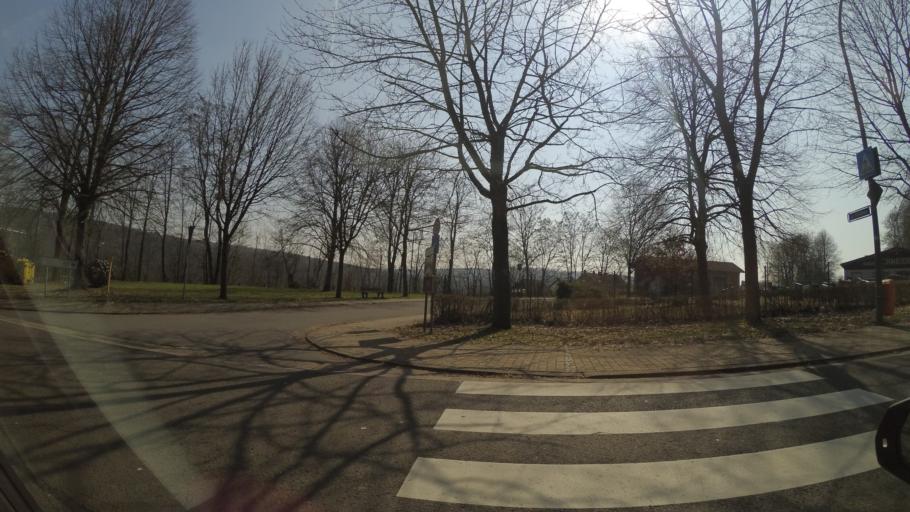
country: DE
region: Saarland
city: Friedrichsthal
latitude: 49.3136
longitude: 7.0790
